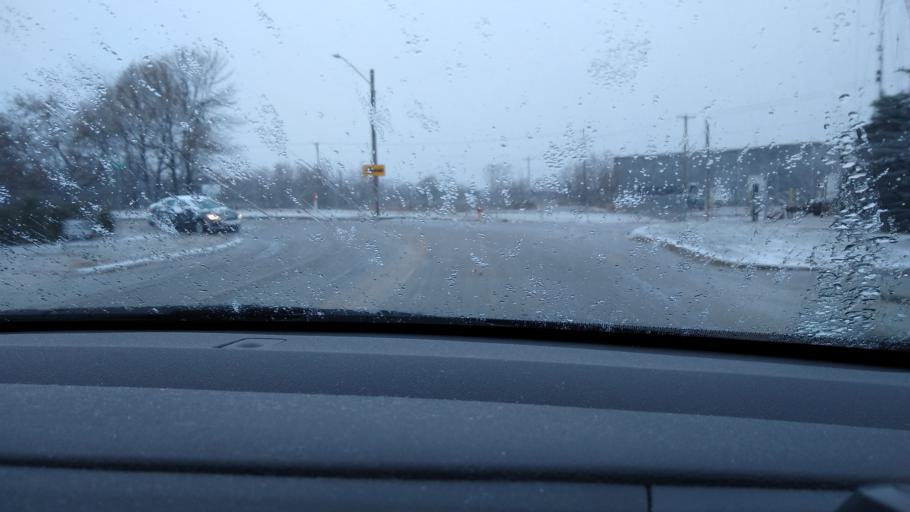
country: US
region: Michigan
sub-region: Delta County
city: Escanaba
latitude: 45.7490
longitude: -87.0612
